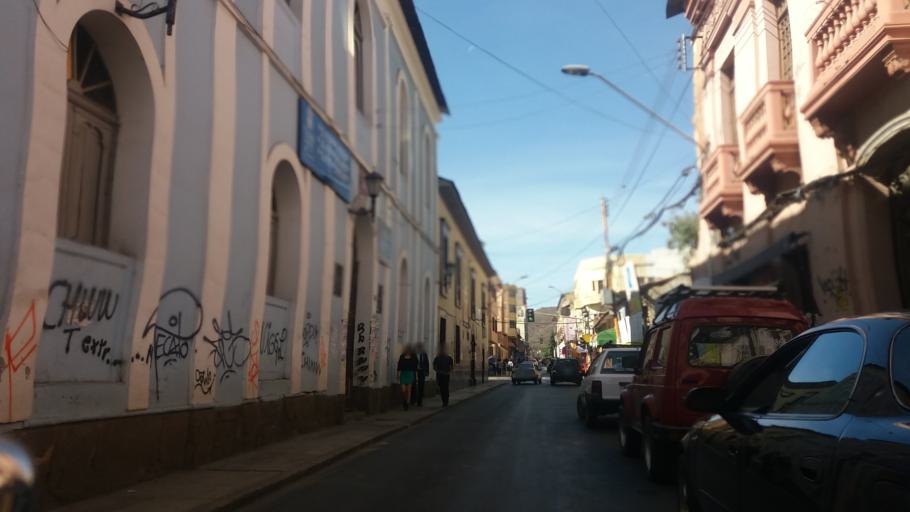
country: BO
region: Cochabamba
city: Cochabamba
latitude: -17.3938
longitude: -66.1537
